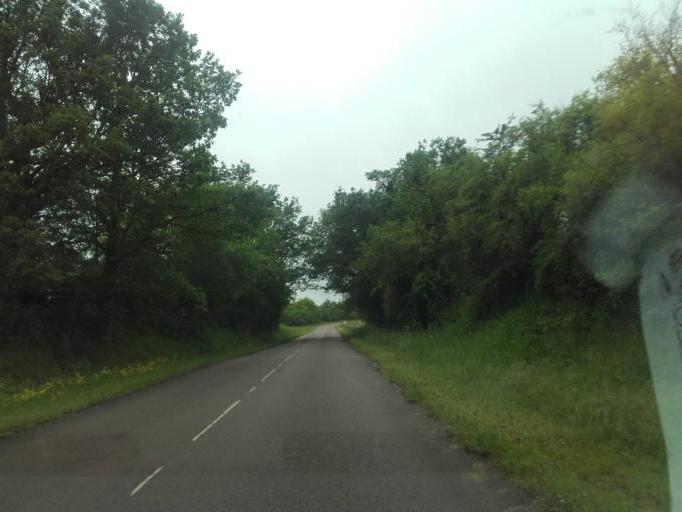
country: FR
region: Bourgogne
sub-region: Departement de la Cote-d'Or
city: Nolay
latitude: 46.9433
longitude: 4.6914
